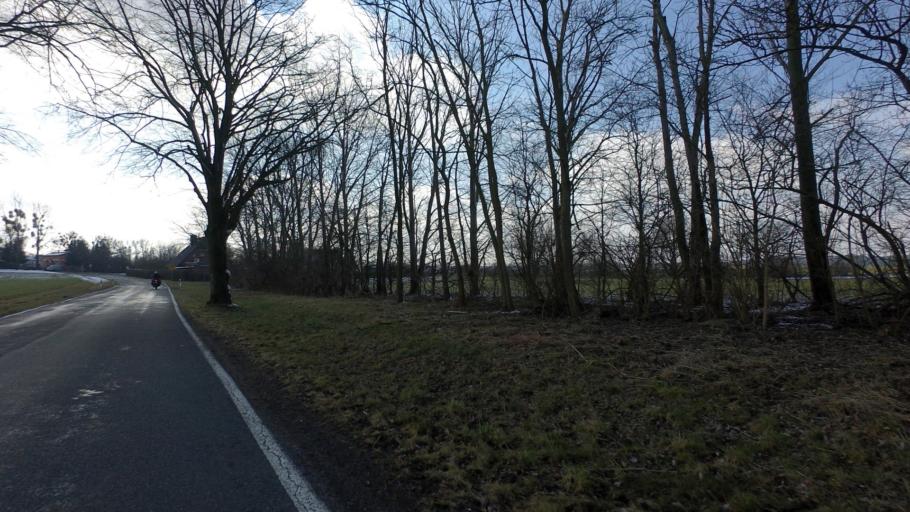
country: DE
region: Brandenburg
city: Werneuchen
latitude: 52.6862
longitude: 13.7293
